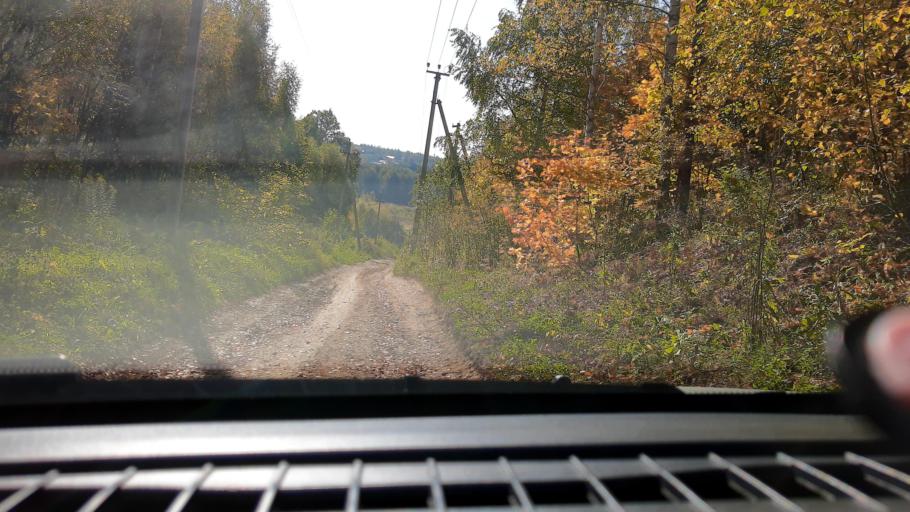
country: RU
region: Nizjnij Novgorod
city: Afonino
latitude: 56.2406
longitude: 44.0588
